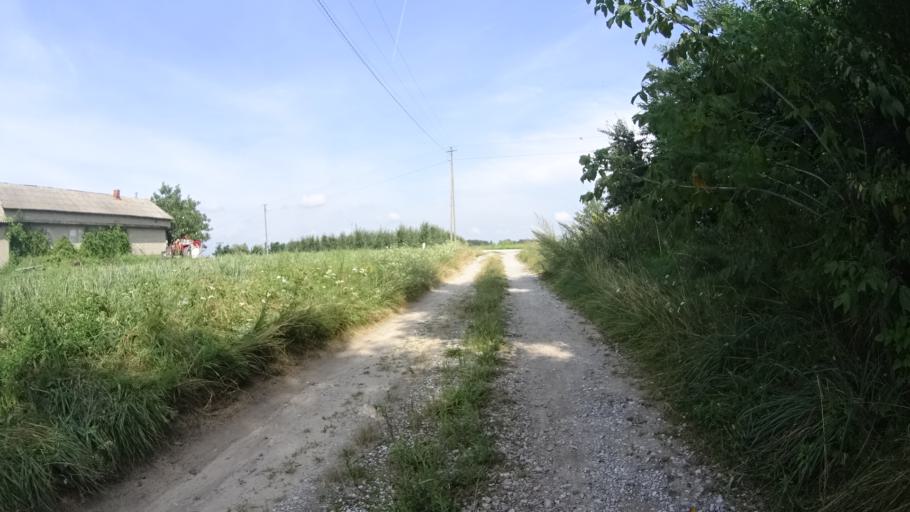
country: PL
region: Masovian Voivodeship
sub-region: Powiat grojecki
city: Goszczyn
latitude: 51.6859
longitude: 20.8421
